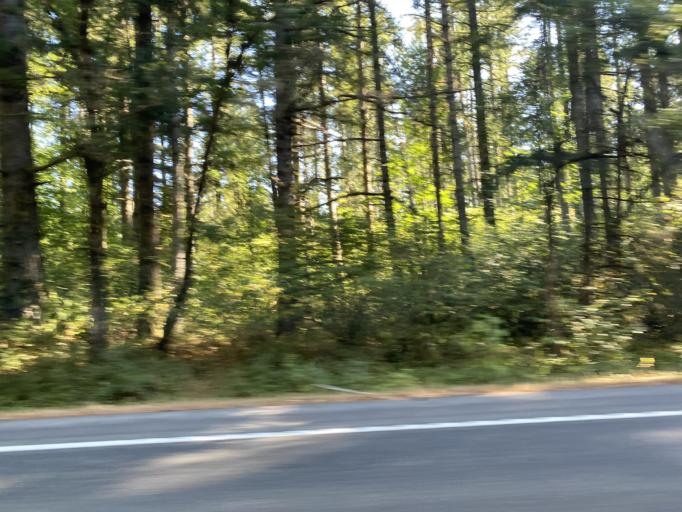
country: US
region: Washington
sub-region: Thurston County
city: Rainier
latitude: 46.9153
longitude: -122.7374
